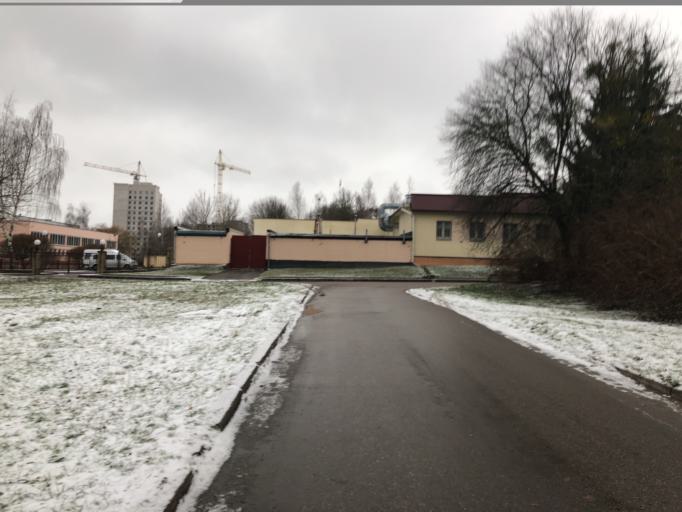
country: BY
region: Grodnenskaya
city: Hrodna
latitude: 53.7006
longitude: 23.8138
